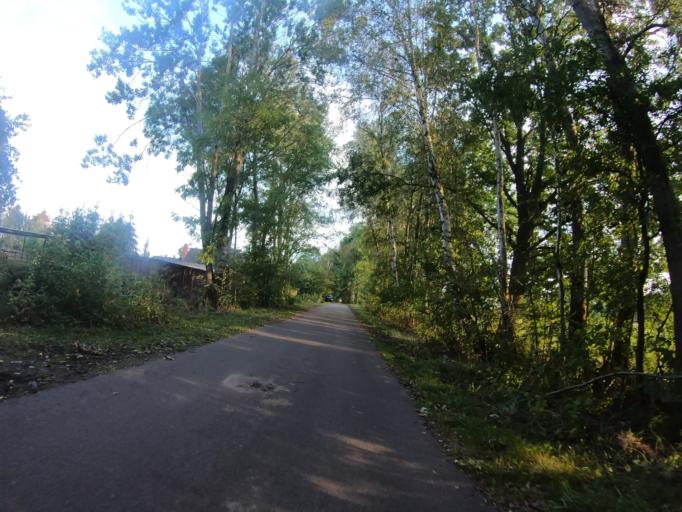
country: DE
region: Lower Saxony
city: Wagenhoff
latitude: 52.5487
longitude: 10.5294
